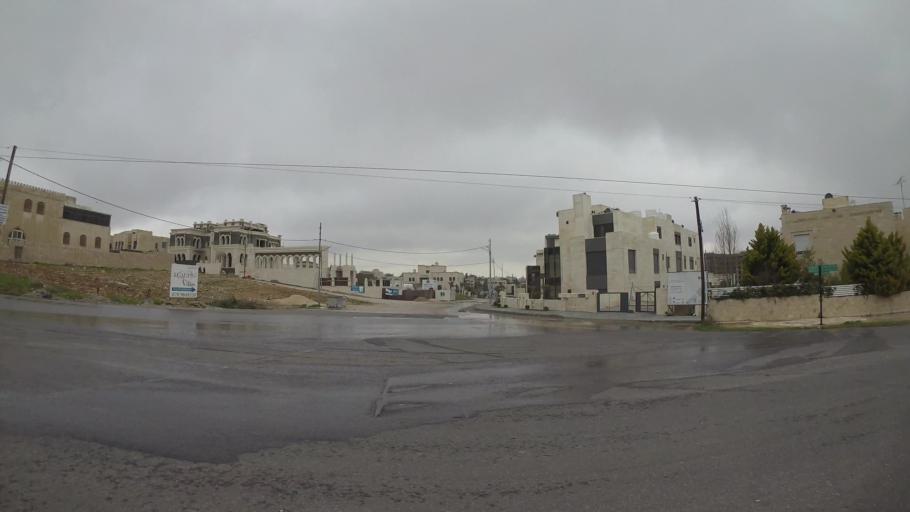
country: JO
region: Amman
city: Al Bunayyat ash Shamaliyah
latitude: 31.9443
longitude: 35.8842
